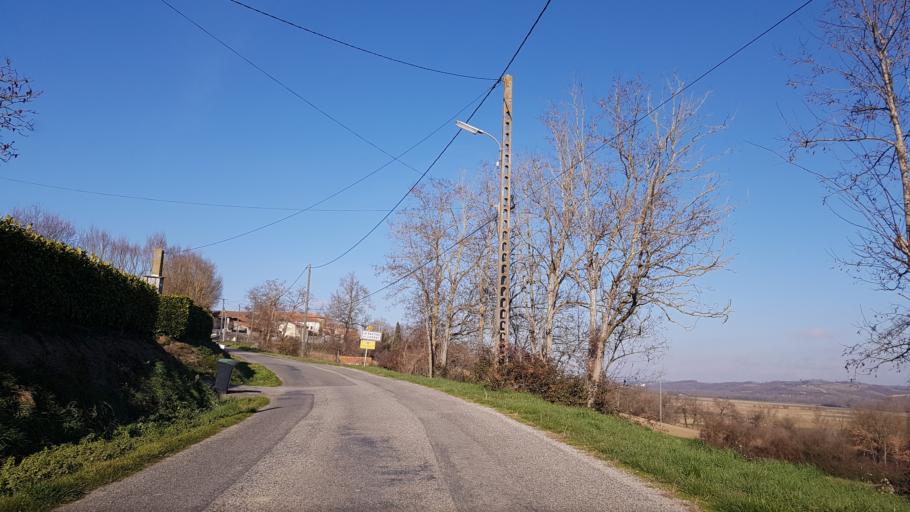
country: FR
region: Midi-Pyrenees
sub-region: Departement de l'Ariege
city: La Tour-du-Crieu
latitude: 43.1395
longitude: 1.7126
